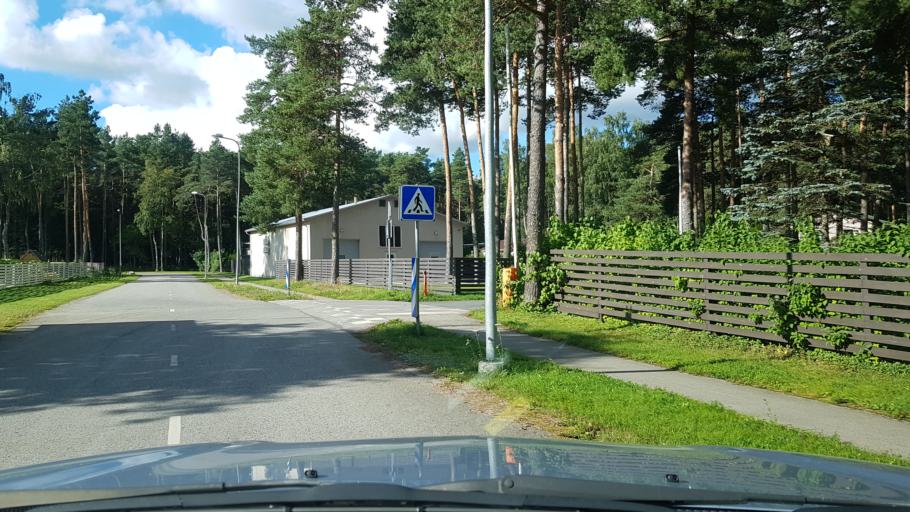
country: EE
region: Harju
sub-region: Tallinna linn
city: Tallinn
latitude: 59.3708
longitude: 24.7639
